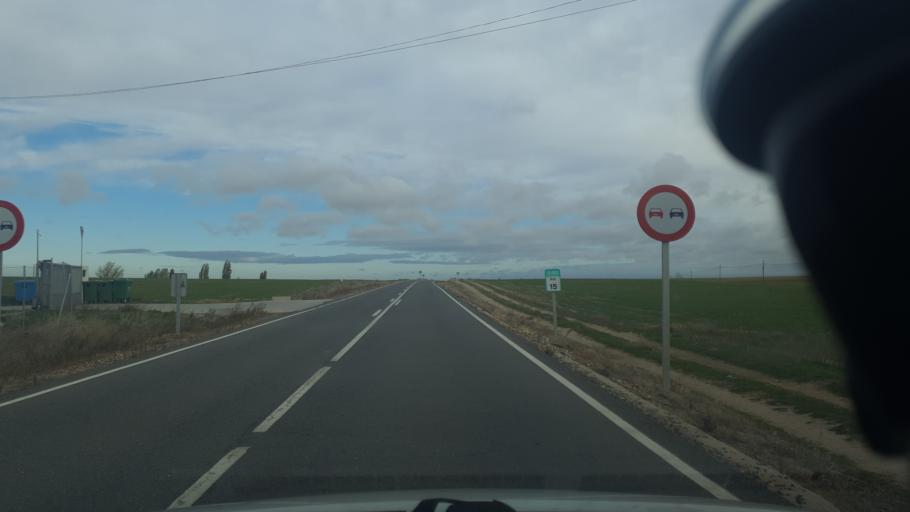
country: ES
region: Castille and Leon
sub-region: Provincia de Avila
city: Gotarrendura
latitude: 40.8080
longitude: -4.7572
